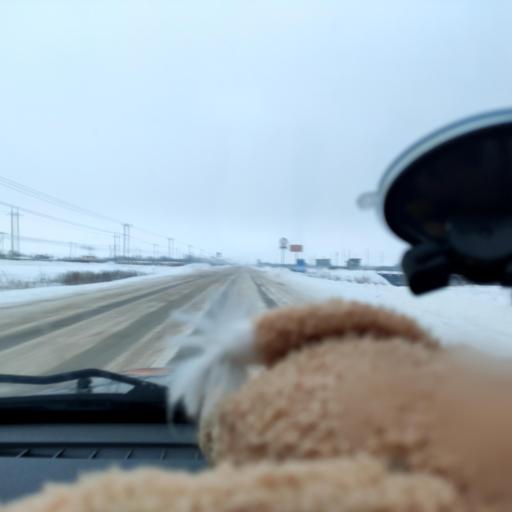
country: RU
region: Samara
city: Podstepki
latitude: 53.5321
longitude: 49.0853
